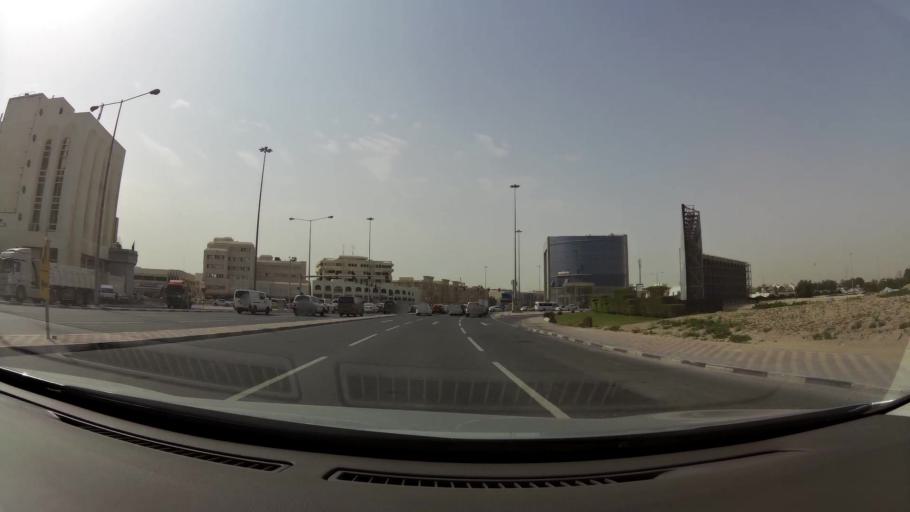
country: QA
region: Baladiyat ad Dawhah
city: Doha
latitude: 25.2815
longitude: 51.4945
